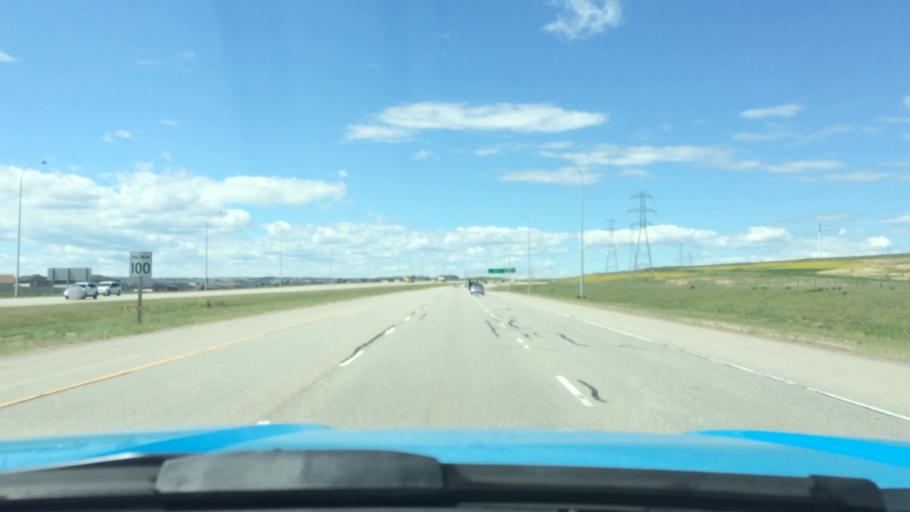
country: CA
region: Alberta
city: Airdrie
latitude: 51.1746
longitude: -114.0516
